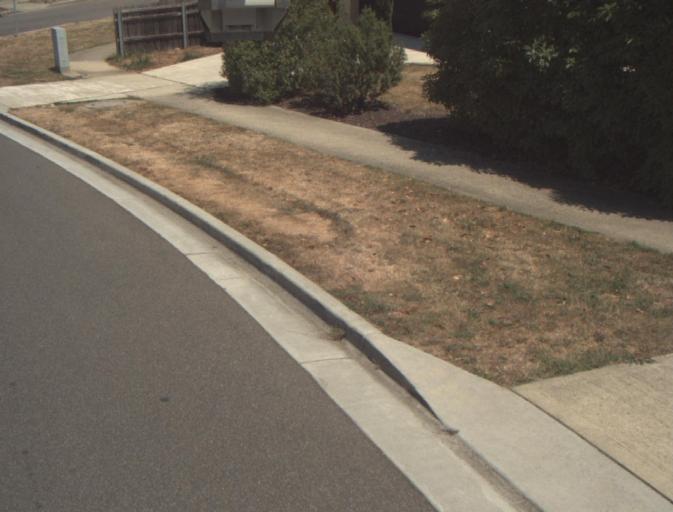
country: AU
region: Tasmania
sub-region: Launceston
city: Summerhill
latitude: -41.4888
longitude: 147.1715
